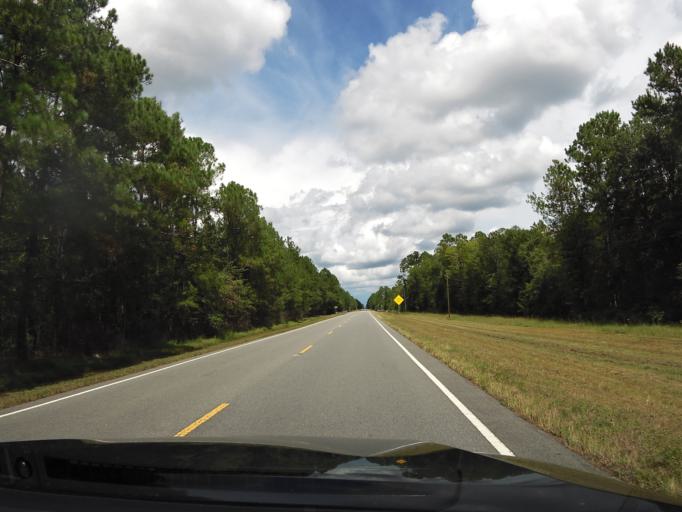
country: US
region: Georgia
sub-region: Brantley County
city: Nahunta
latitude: 31.0445
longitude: -82.0187
